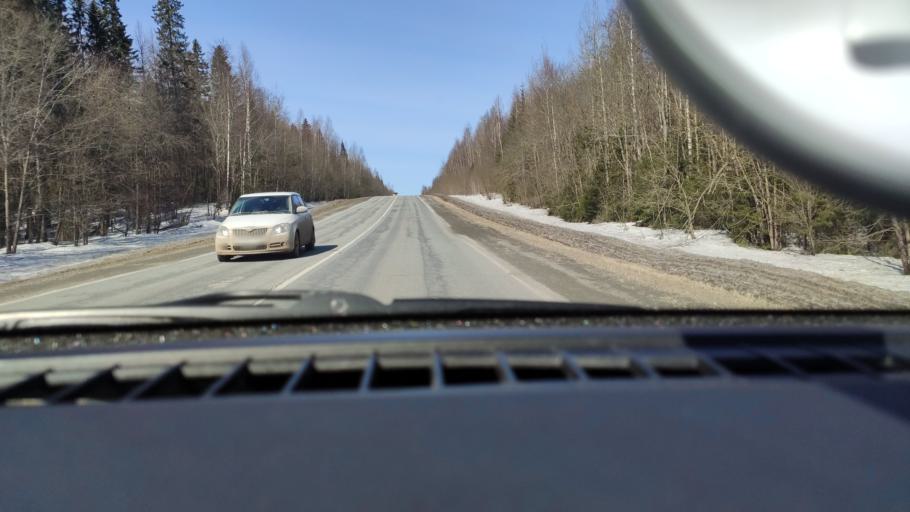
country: RU
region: Perm
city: Perm
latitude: 58.1722
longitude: 56.2334
